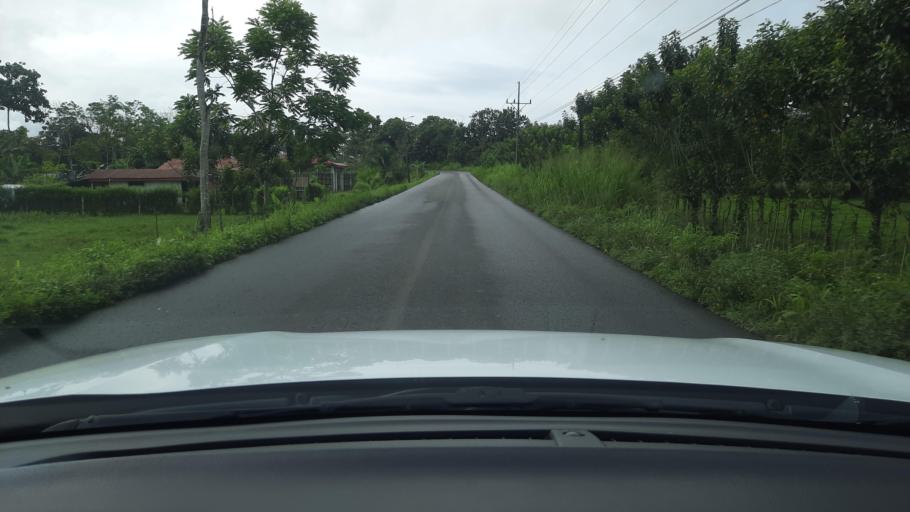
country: CR
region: Alajuela
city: San Jose
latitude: 10.9289
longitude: -85.0969
